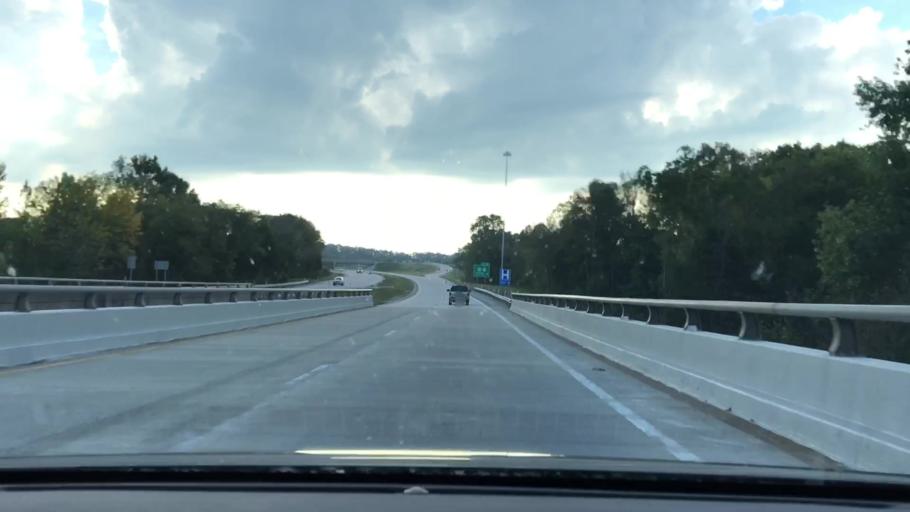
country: US
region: Kentucky
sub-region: Barren County
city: Glasgow
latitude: 36.9954
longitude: -85.9890
